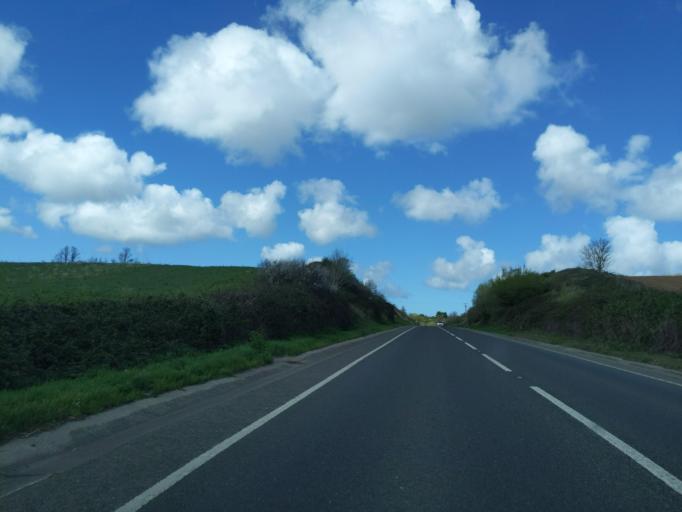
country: GB
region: England
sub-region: Cornwall
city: Wadebridge
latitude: 50.5162
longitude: -4.8191
